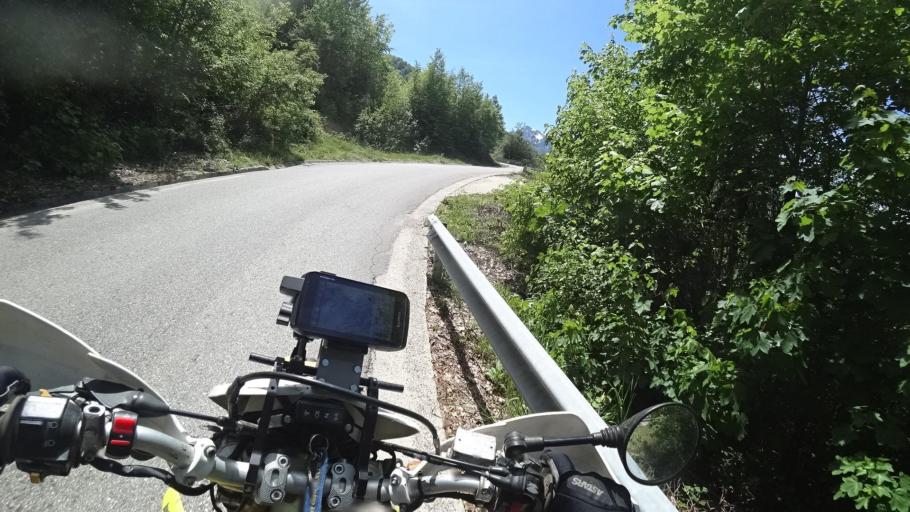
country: BA
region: Federation of Bosnia and Herzegovina
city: Polje-Bijela
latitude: 43.6106
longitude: 17.9815
